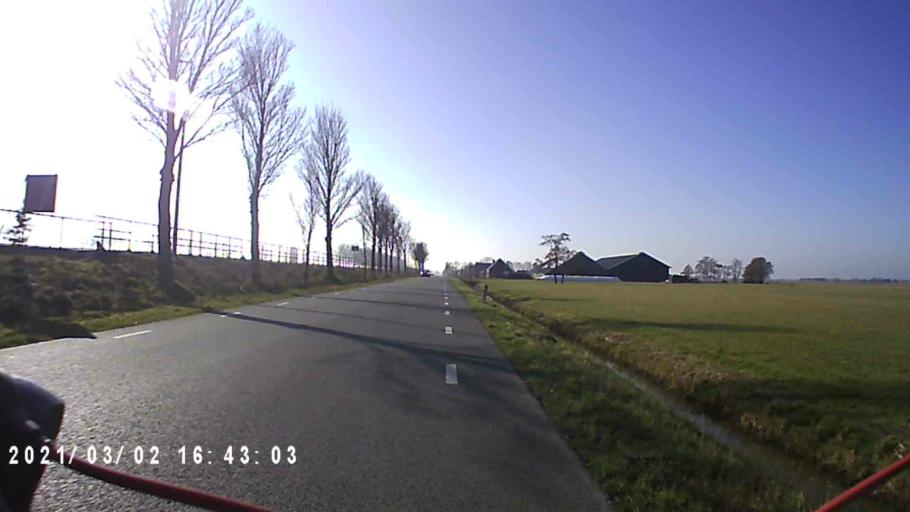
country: NL
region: Groningen
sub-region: Gemeente Zuidhorn
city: Grijpskerk
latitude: 53.2489
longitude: 6.3083
